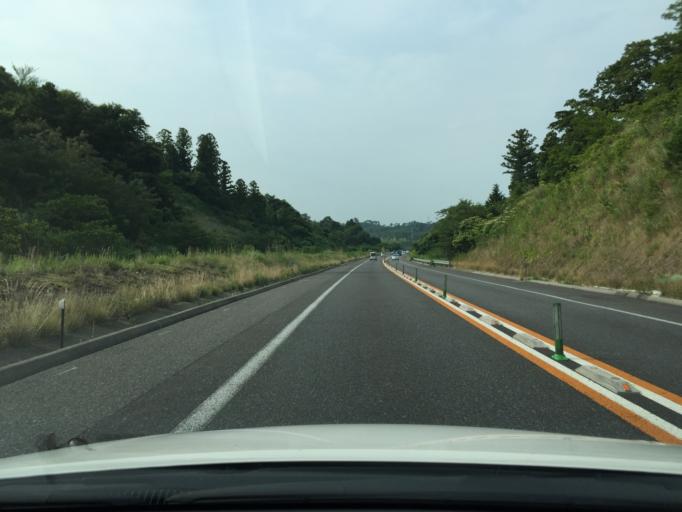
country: JP
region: Fukushima
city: Iwaki
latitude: 37.1621
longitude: 140.9665
